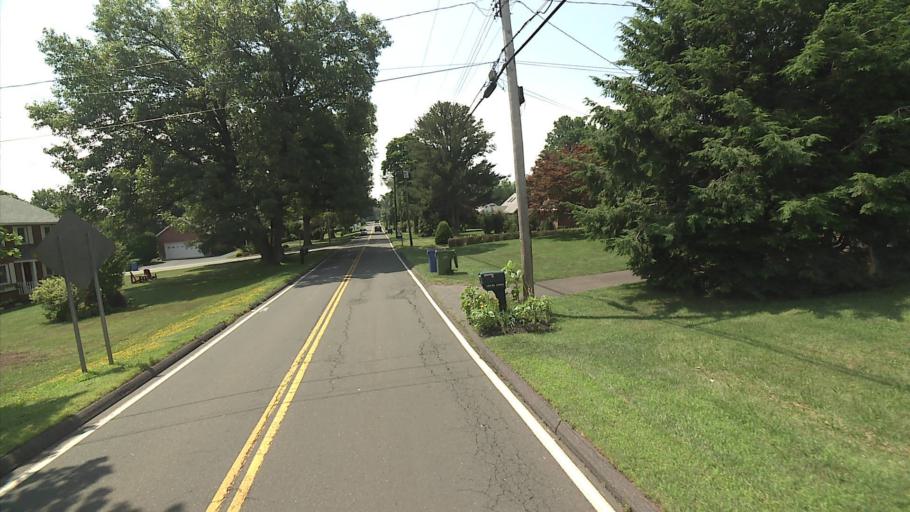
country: US
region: Connecticut
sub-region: Middlesex County
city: Middletown
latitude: 41.5515
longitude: -72.7011
